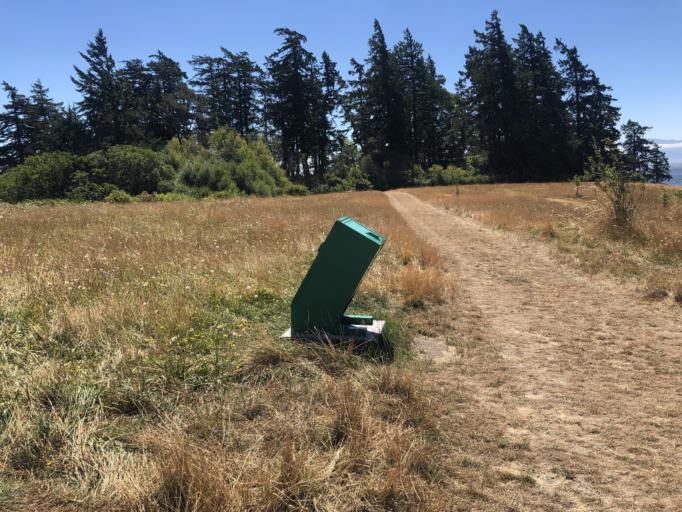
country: CA
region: British Columbia
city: Metchosin
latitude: 48.3854
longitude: -123.5071
